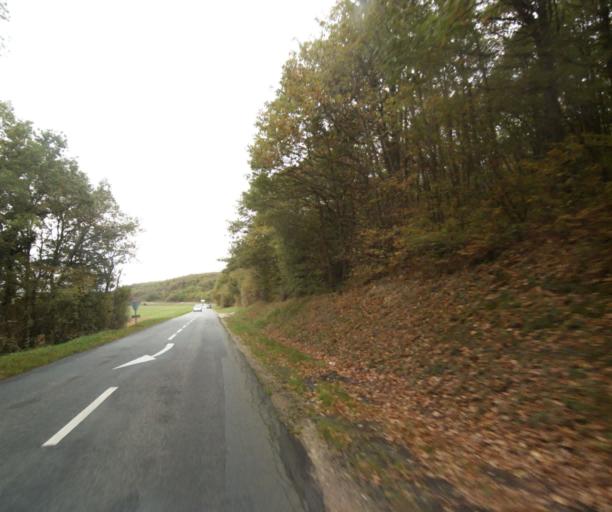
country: FR
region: Centre
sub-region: Departement d'Eure-et-Loir
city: Vert-en-Drouais
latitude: 48.7437
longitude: 1.3224
